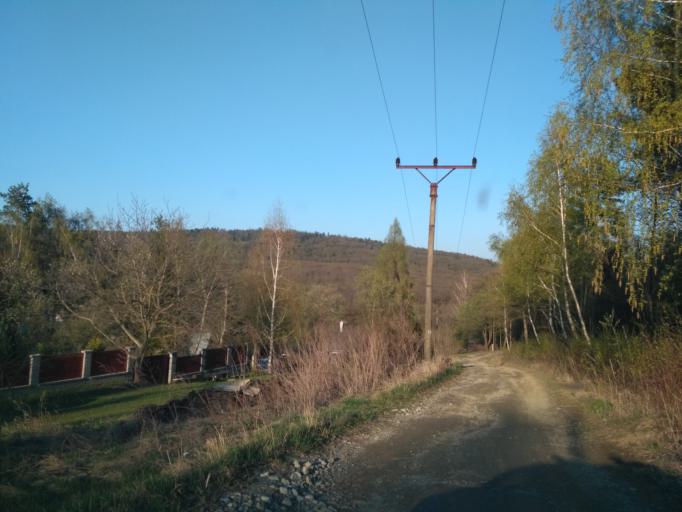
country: SK
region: Kosicky
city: Kosice
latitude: 48.7333
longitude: 21.1534
